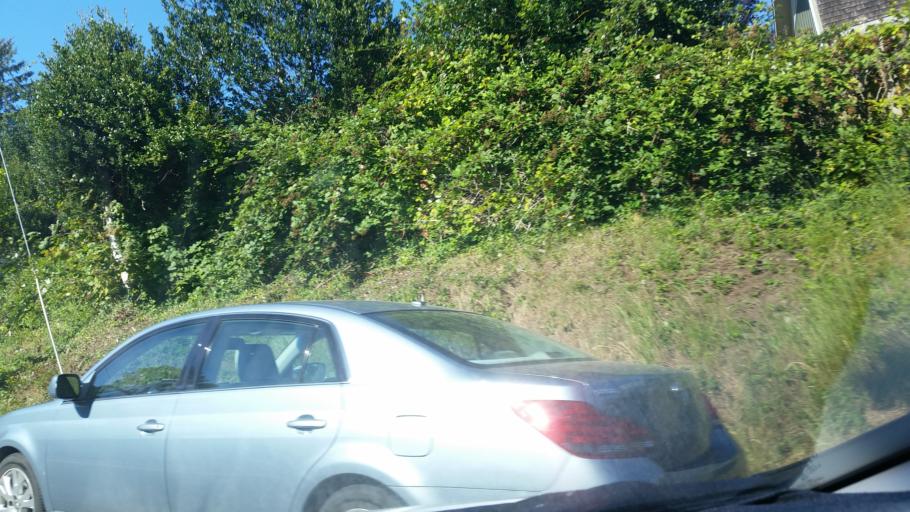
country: US
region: Oregon
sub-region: Clatsop County
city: Astoria
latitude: 46.1825
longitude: -123.8550
